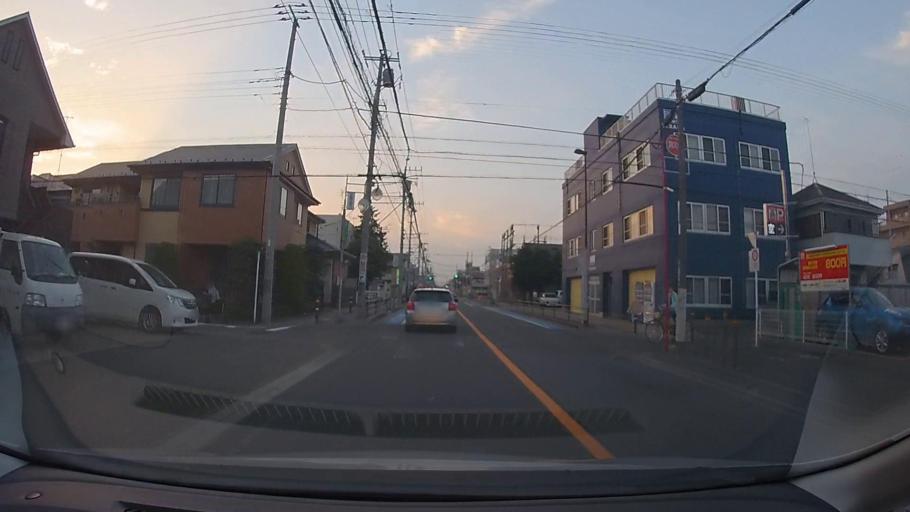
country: JP
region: Kanagawa
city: Minami-rinkan
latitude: 35.4834
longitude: 139.4508
